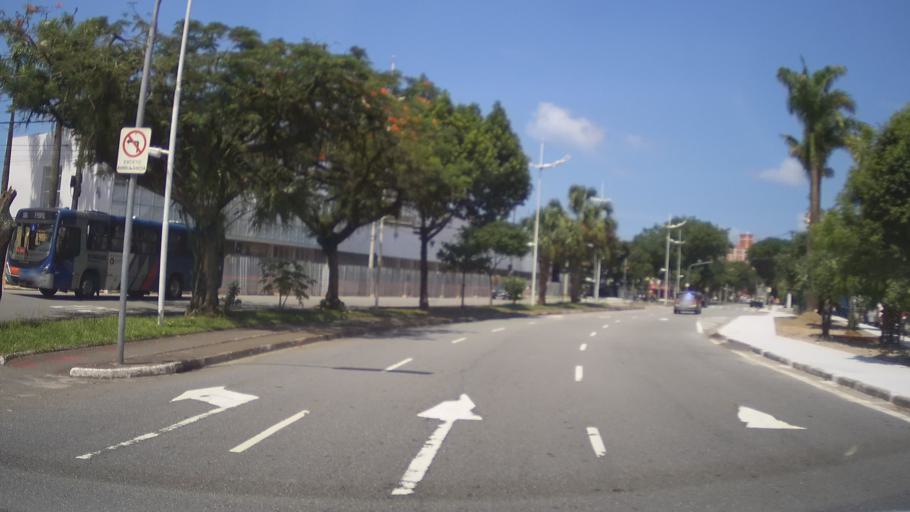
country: BR
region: Sao Paulo
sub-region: Santos
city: Santos
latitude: -23.9709
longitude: -46.3024
